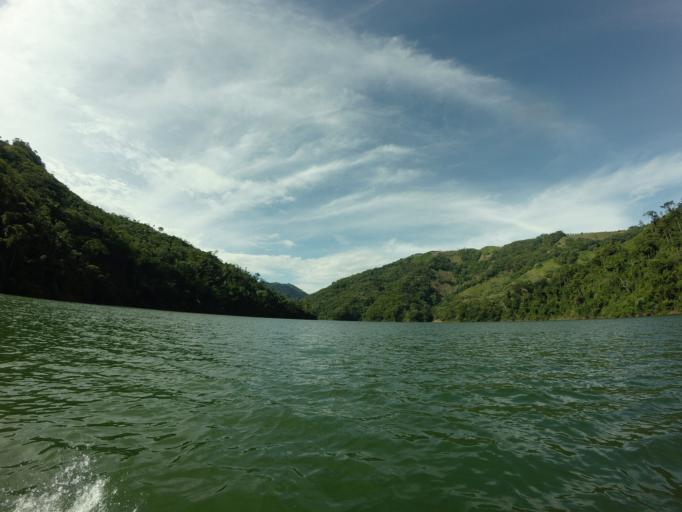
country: CO
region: Caldas
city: Norcasia
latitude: 5.5425
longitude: -74.9151
